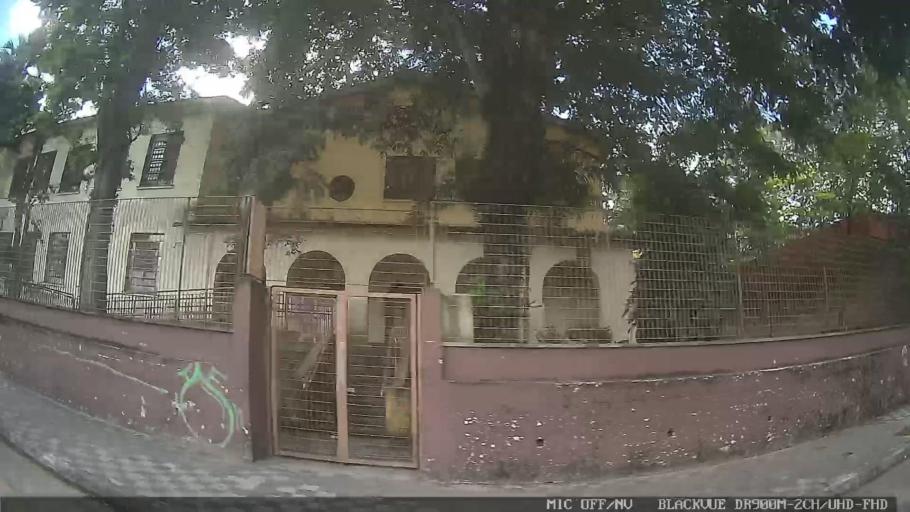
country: BR
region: Sao Paulo
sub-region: Jacarei
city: Jacarei
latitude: -23.3016
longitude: -45.9586
